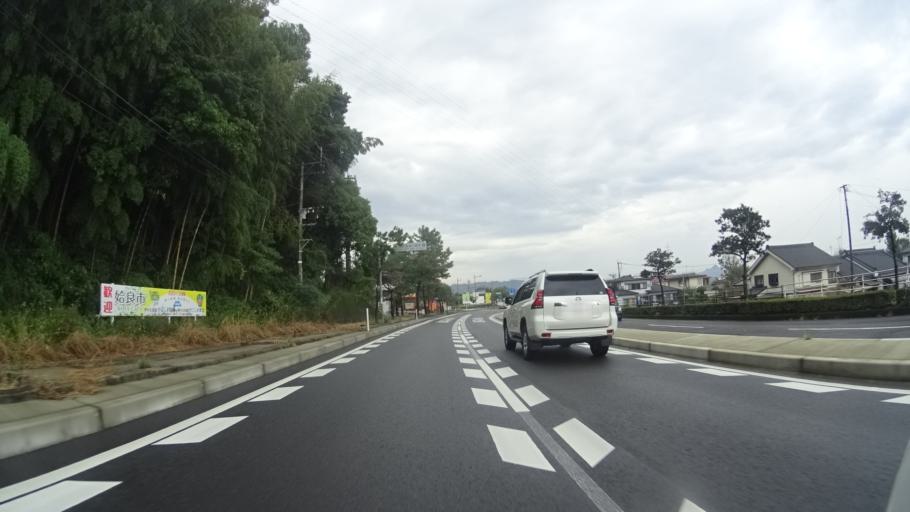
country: JP
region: Kagoshima
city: Kajiki
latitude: 31.7017
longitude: 130.6114
